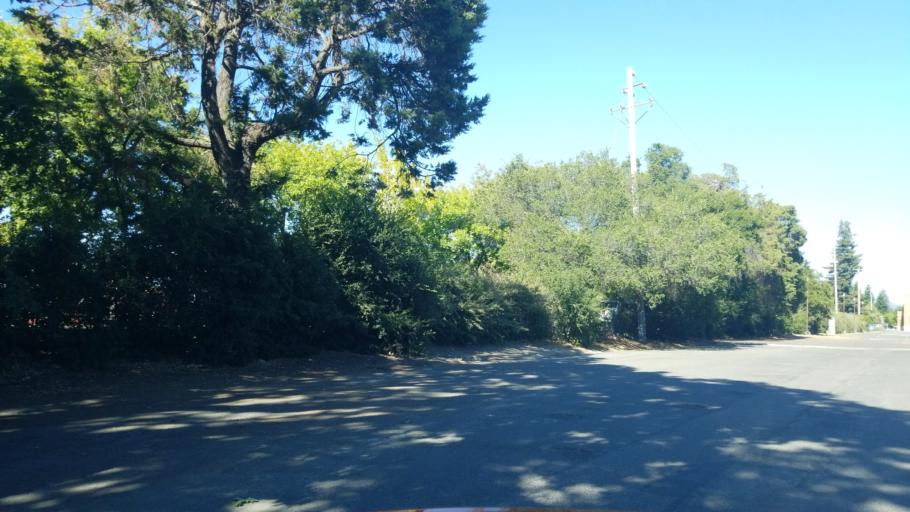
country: US
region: California
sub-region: Sonoma County
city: Santa Rosa
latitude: 38.4529
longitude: -122.7208
